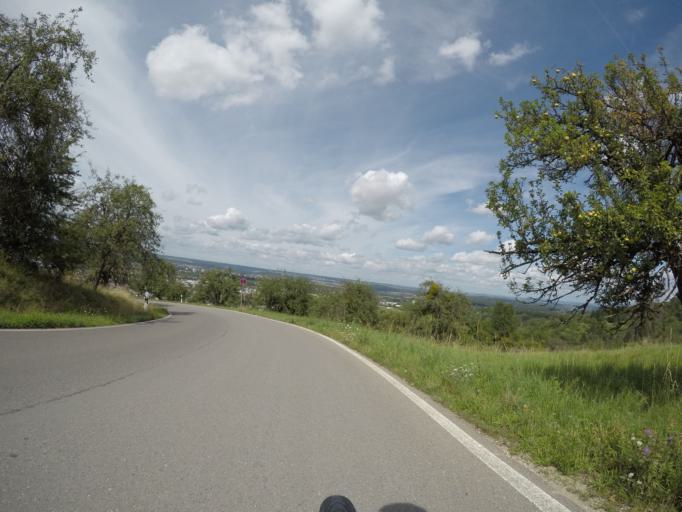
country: DE
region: Baden-Wuerttemberg
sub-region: Tuebingen Region
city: Eningen unter Achalm
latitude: 48.4969
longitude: 9.2346
